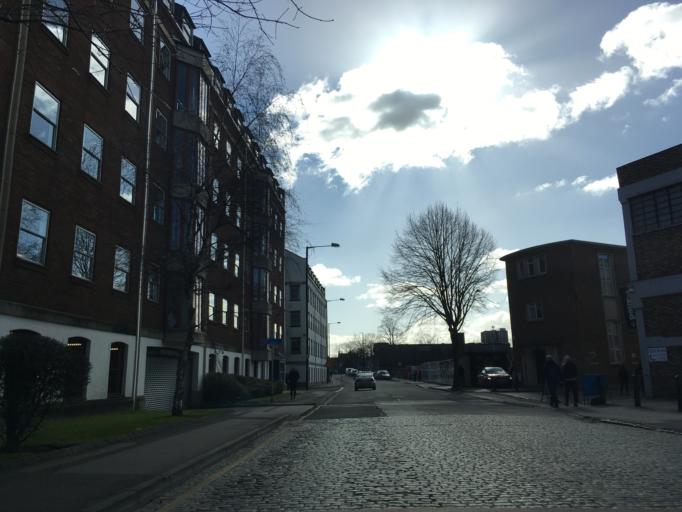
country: GB
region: England
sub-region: Bristol
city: Bristol
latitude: 51.4483
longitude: -2.5968
